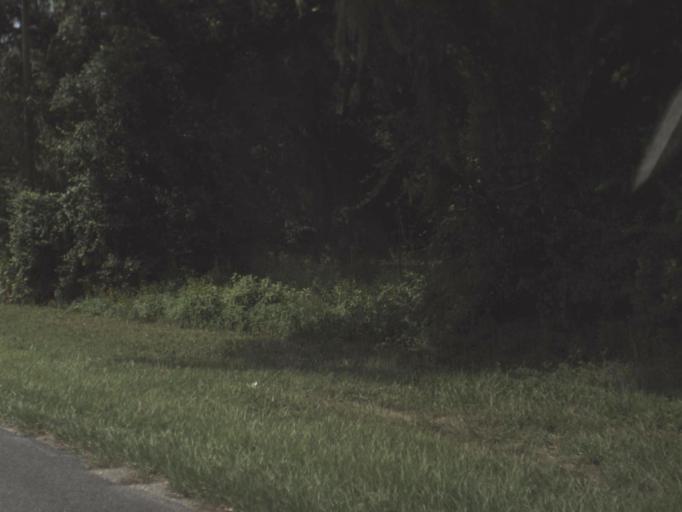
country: US
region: Florida
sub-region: Citrus County
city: Inverness Highlands North
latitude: 28.8651
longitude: -82.3568
